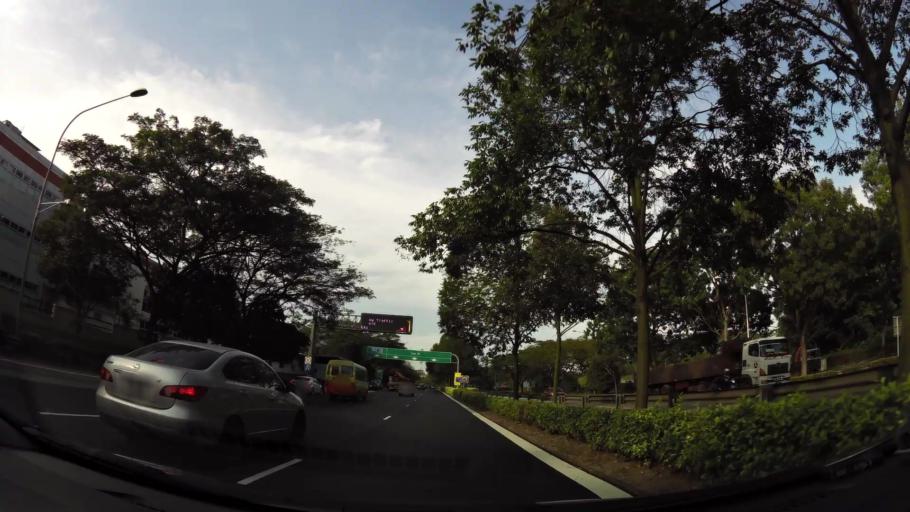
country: MY
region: Johor
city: Johor Bahru
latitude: 1.3296
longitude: 103.6708
